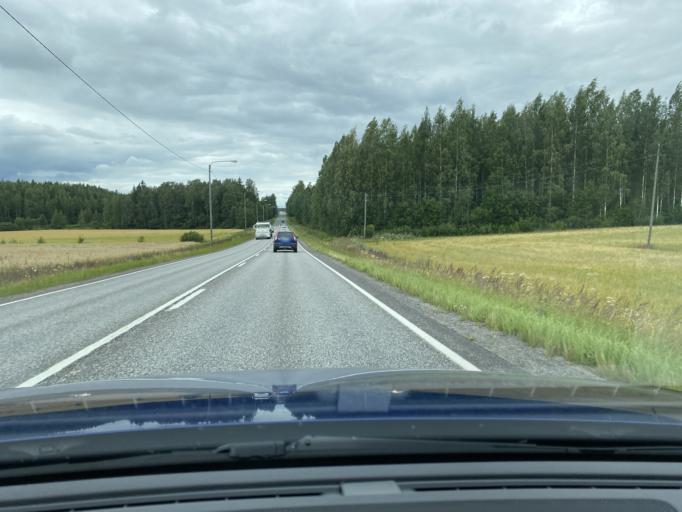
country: FI
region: Uusimaa
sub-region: Helsinki
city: Karkkila
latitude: 60.4971
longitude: 24.2762
